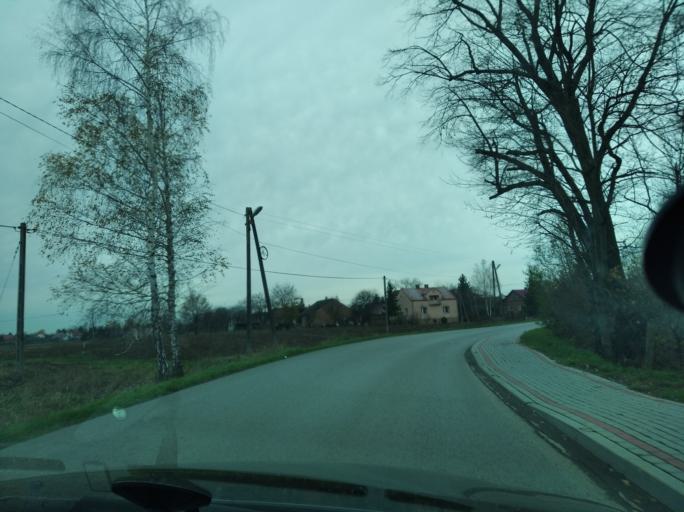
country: PL
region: Subcarpathian Voivodeship
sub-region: Powiat lancucki
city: Rogozno
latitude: 50.0988
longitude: 22.4026
